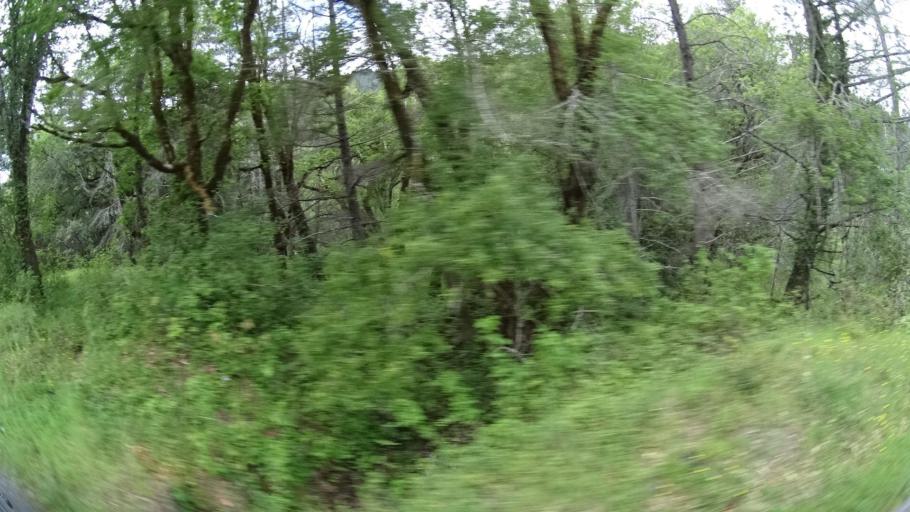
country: US
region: California
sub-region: Humboldt County
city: Redway
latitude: 40.2133
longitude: -123.5959
